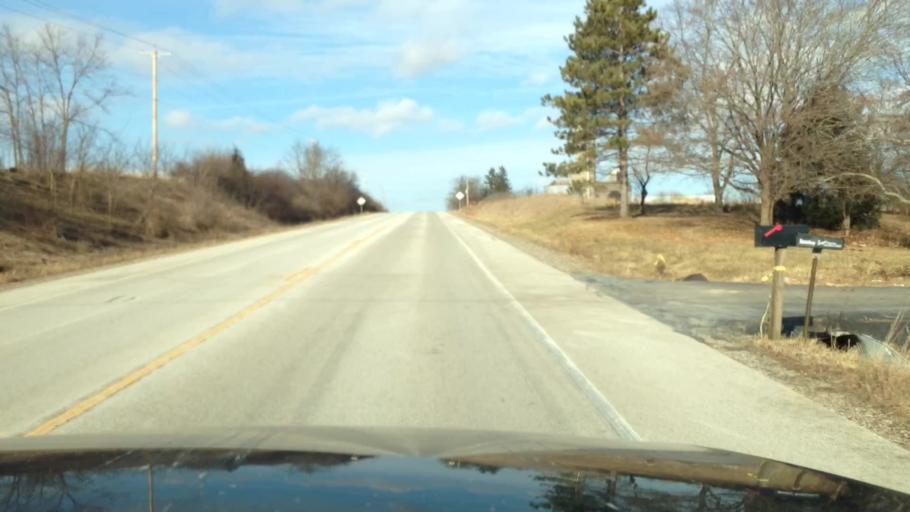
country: US
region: Wisconsin
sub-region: Walworth County
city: Lake Geneva
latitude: 42.6475
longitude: -88.4136
